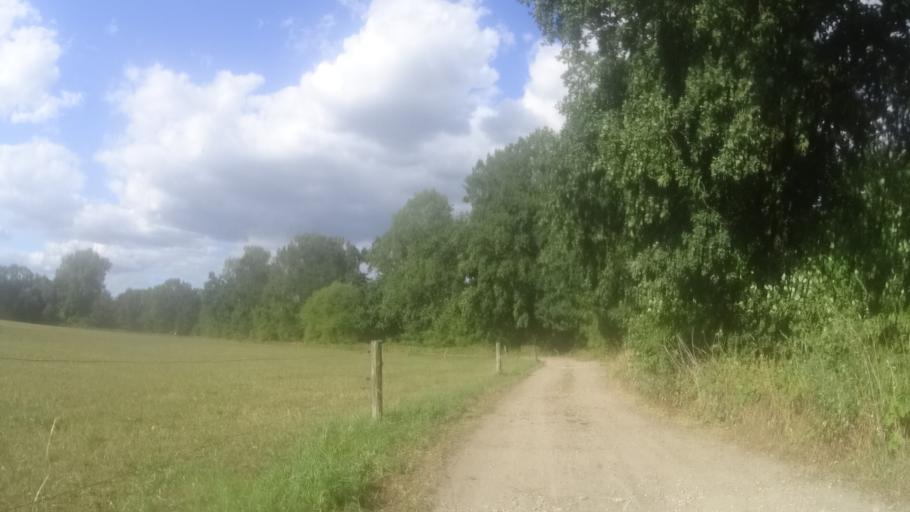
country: CZ
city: Albrechtice nad Orlici
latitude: 50.1596
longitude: 16.0416
